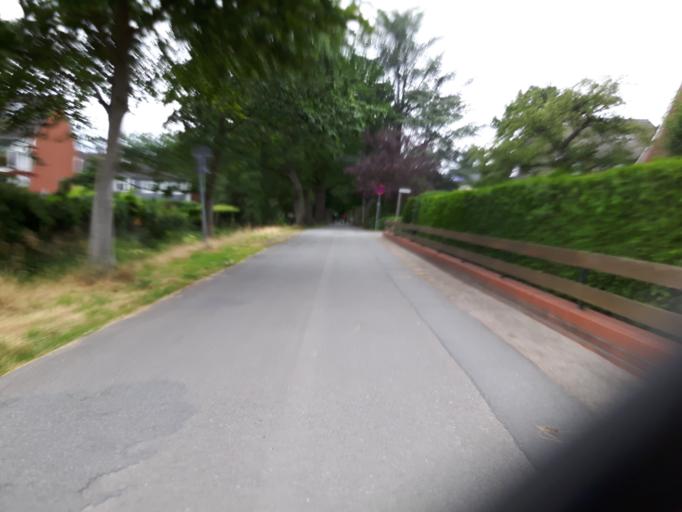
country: DE
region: Lower Saxony
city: Stuhr
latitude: 53.0325
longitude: 8.7026
